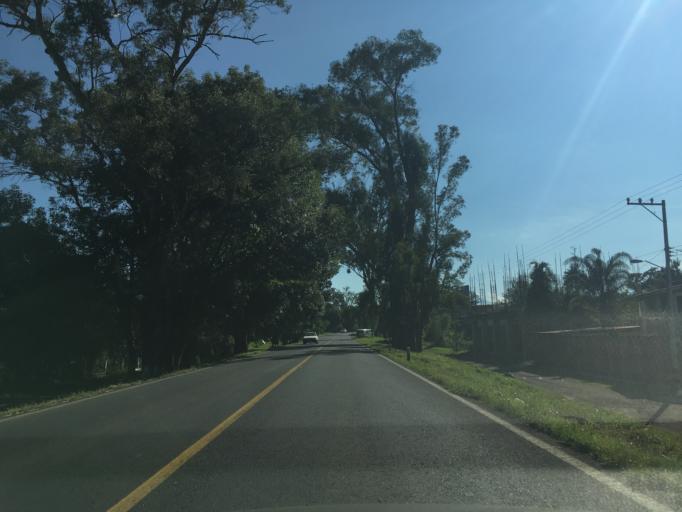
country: MX
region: Mexico
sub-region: Chalco
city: Chilchota
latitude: 19.8504
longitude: -102.1239
